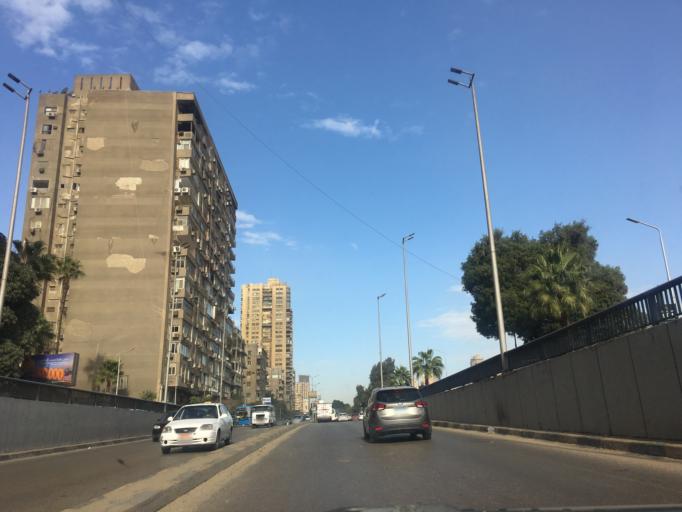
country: EG
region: Al Jizah
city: Al Jizah
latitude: 30.0418
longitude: 31.2195
